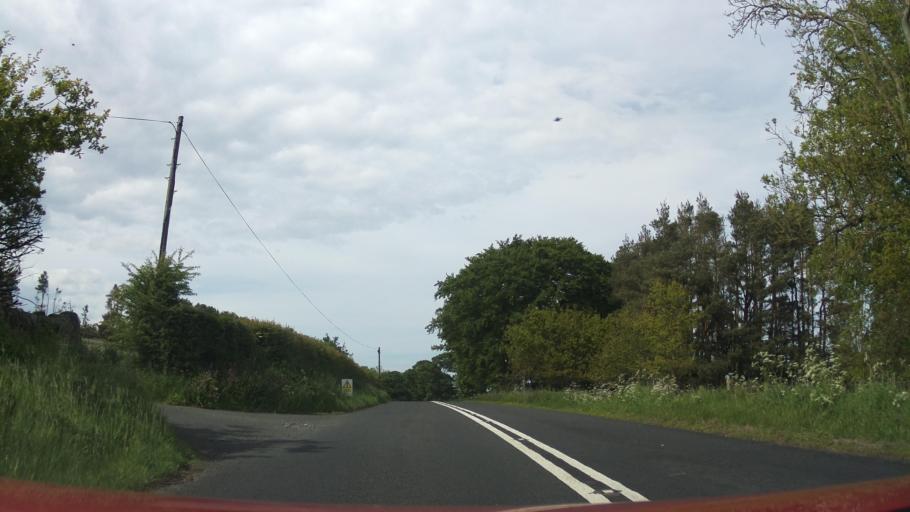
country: GB
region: England
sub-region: Northumberland
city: Alnwick
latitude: 55.4514
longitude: -1.7111
